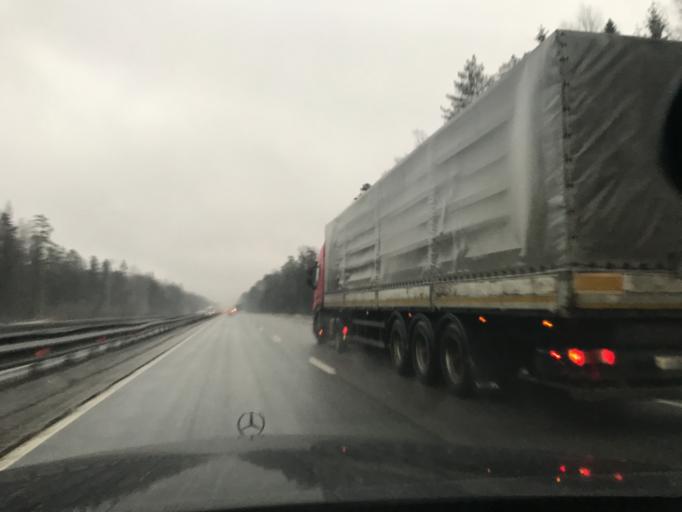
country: RU
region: Vladimir
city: Stepantsevo
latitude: 56.2264
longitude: 41.6448
